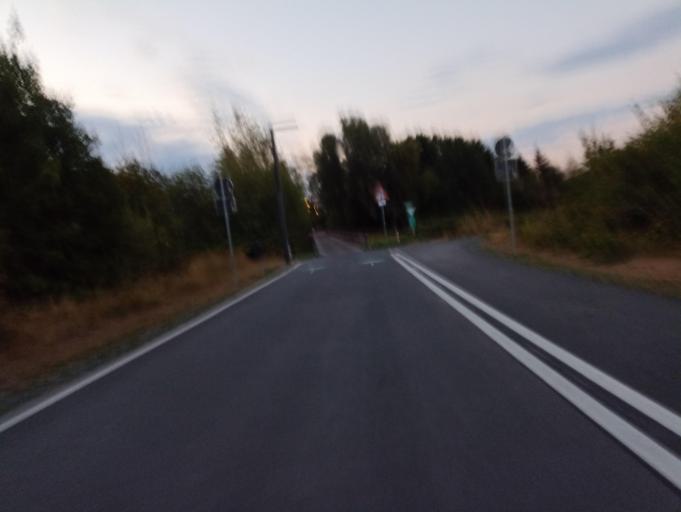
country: DE
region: Hesse
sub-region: Regierungsbezirk Darmstadt
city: Egelsbach
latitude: 49.9744
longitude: 8.6546
